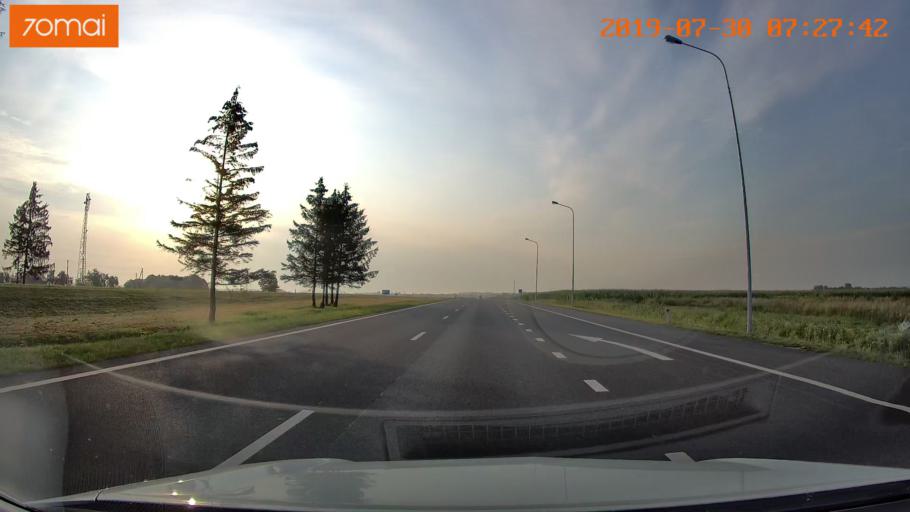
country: RU
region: Kaliningrad
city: Gvardeysk
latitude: 54.6810
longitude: 20.8937
